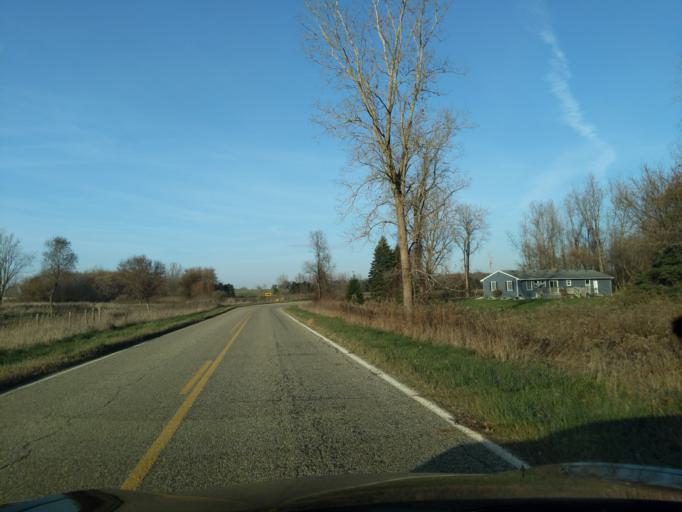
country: US
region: Michigan
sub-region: Clinton County
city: Bath
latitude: 42.7972
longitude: -84.5107
